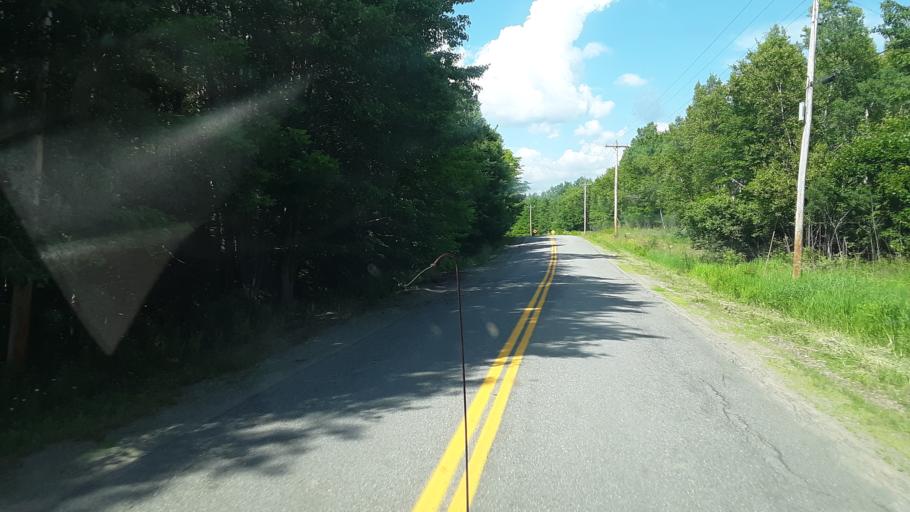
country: US
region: Maine
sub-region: Washington County
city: Calais
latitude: 45.1036
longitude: -67.5099
